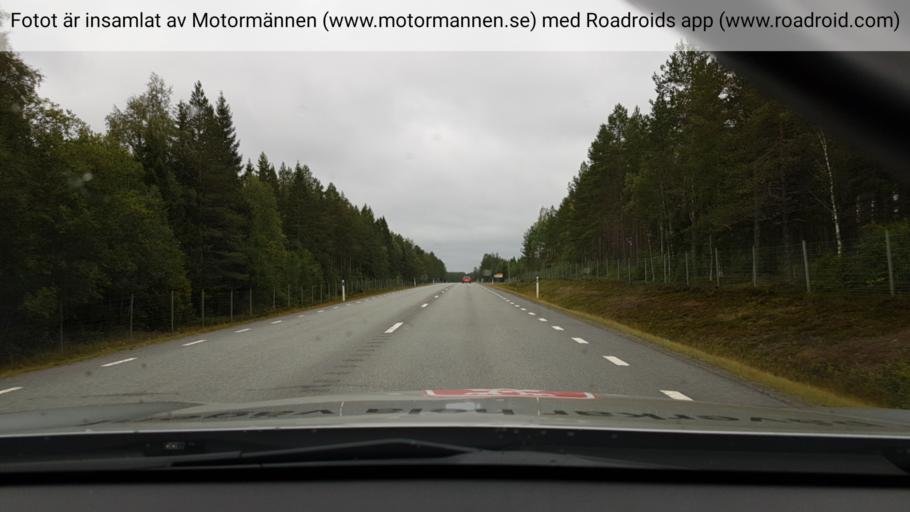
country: SE
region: Vaesterbotten
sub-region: Robertsfors Kommun
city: Robertsfors
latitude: 64.0548
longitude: 20.8481
